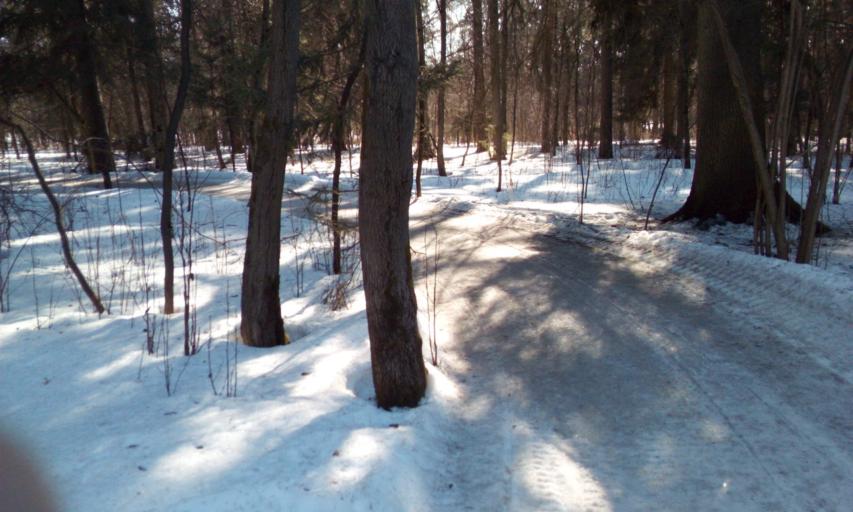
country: RU
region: Moscow
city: Novo-Peredelkino
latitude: 55.6640
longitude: 37.3465
